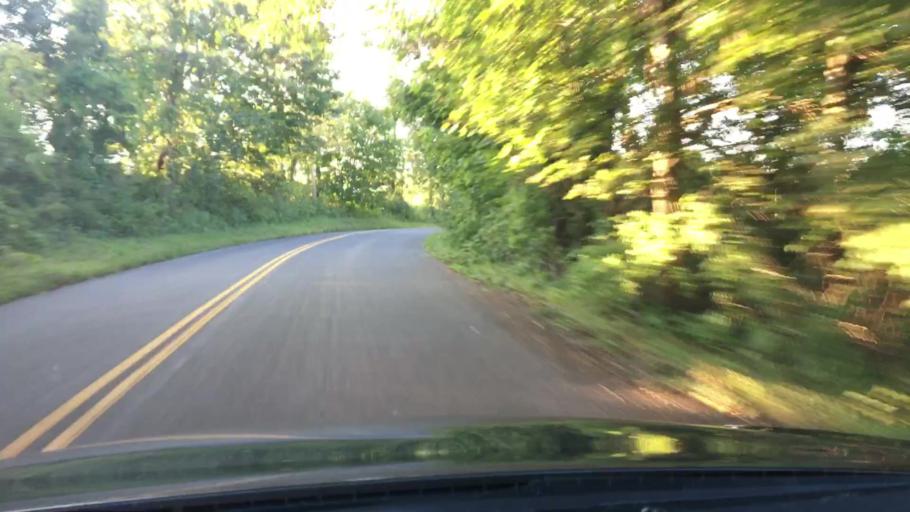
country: US
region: Connecticut
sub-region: Litchfield County
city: New Milford
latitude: 41.6060
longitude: -73.3732
